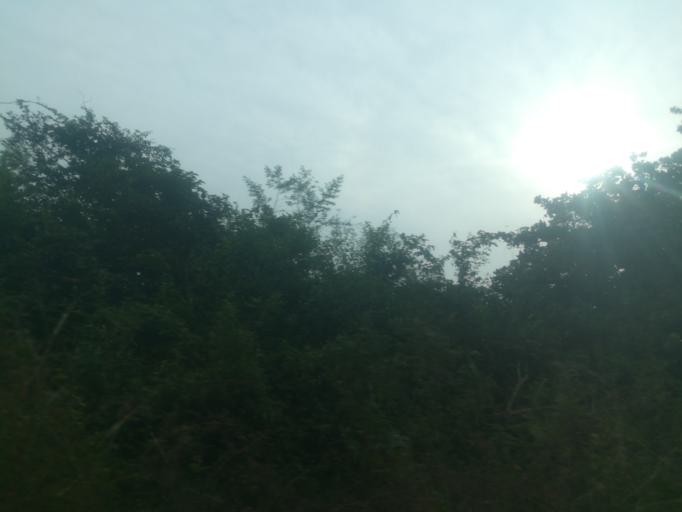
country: NG
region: Ogun
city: Ayetoro
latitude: 7.2827
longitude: 3.0897
